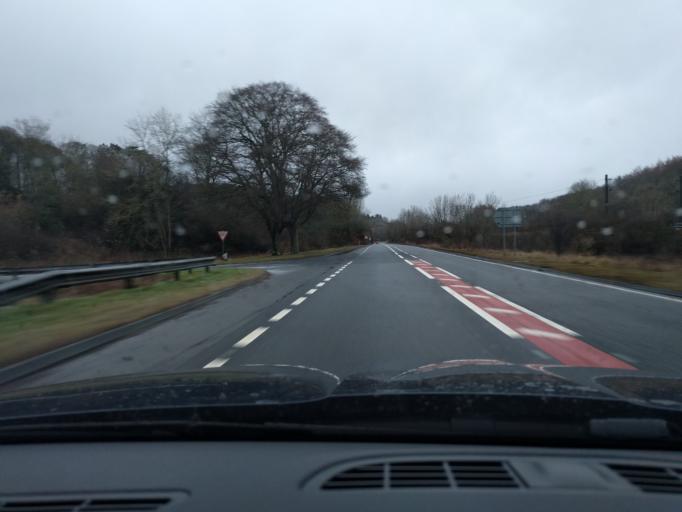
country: GB
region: Scotland
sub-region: The Scottish Borders
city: Chirnside
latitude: 55.8820
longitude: -2.2908
